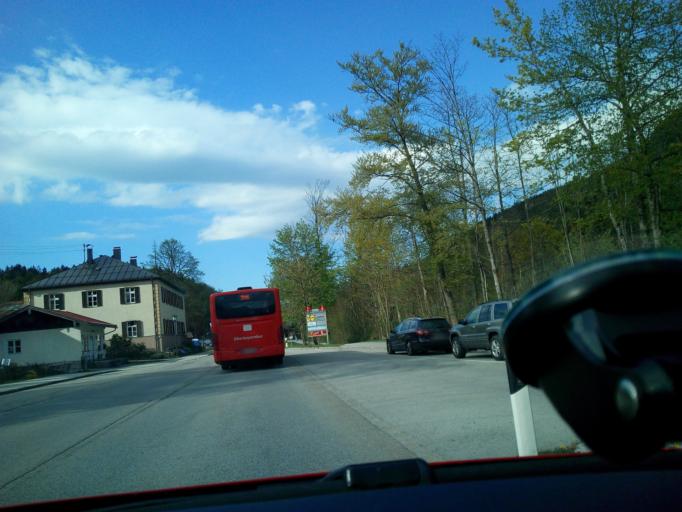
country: DE
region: Bavaria
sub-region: Upper Bavaria
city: Kreuth
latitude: 47.6426
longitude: 11.7449
